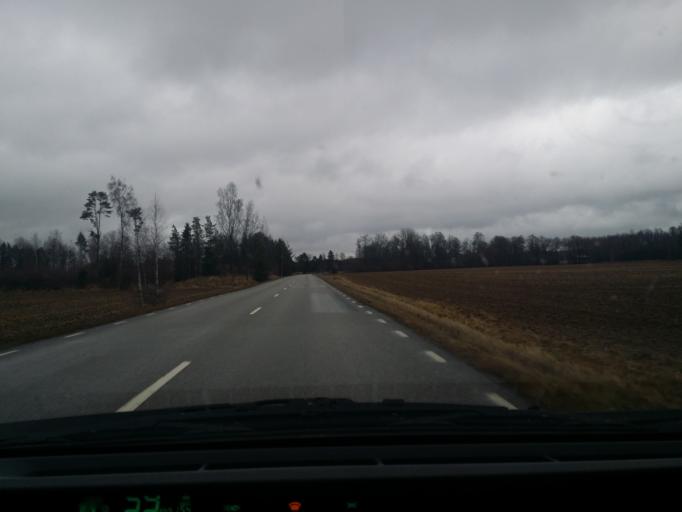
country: SE
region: Vaestmanland
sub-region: Vasteras
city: Skultuna
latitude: 59.7834
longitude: 16.4637
